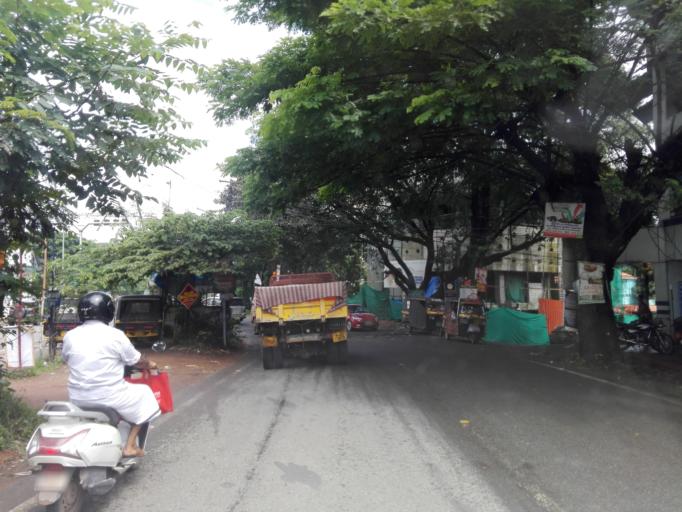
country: IN
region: Kerala
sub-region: Ernakulam
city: Elur
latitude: 10.0231
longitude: 76.3411
